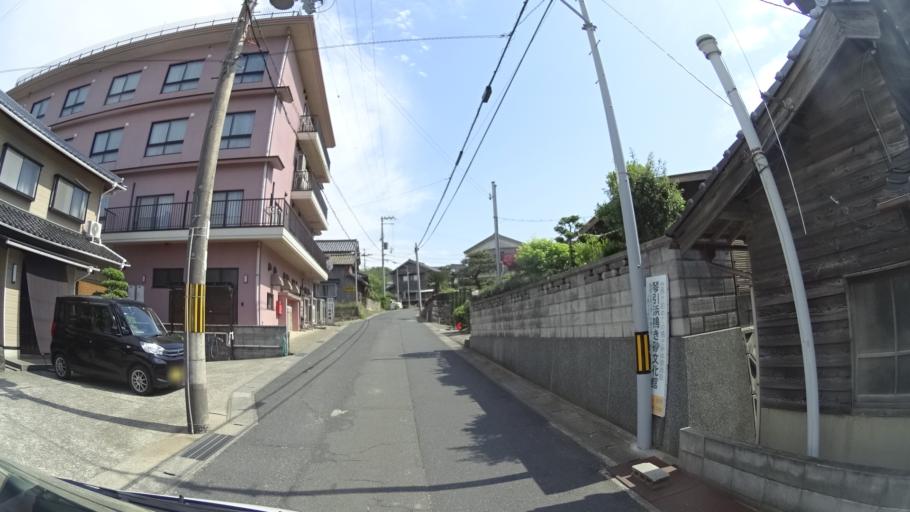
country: JP
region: Kyoto
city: Miyazu
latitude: 35.6983
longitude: 135.0548
